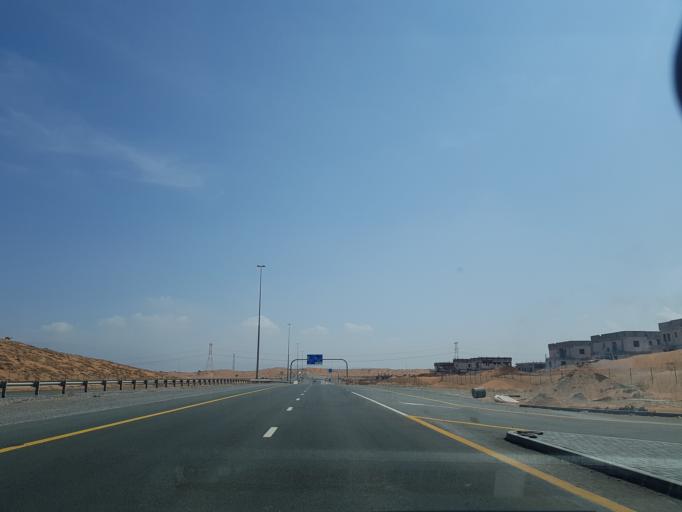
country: AE
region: Ra's al Khaymah
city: Ras al-Khaimah
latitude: 25.6692
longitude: 55.8874
